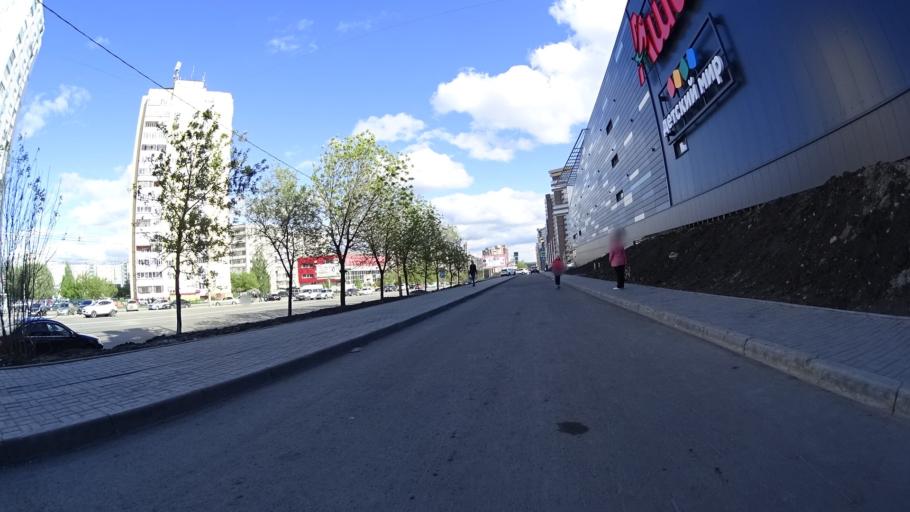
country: RU
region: Chelyabinsk
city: Roshchino
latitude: 55.1813
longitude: 61.2935
